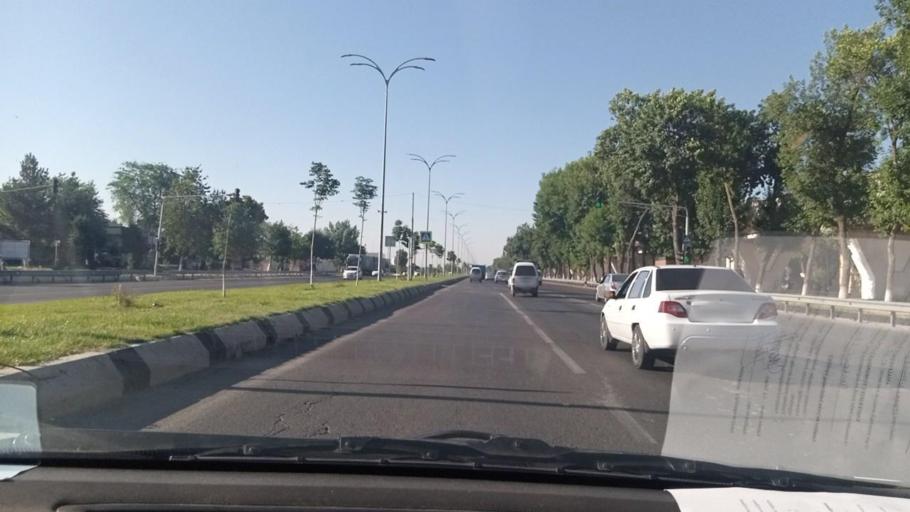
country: UZ
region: Toshkent Shahri
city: Bektemir
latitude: 41.2864
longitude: 69.3599
